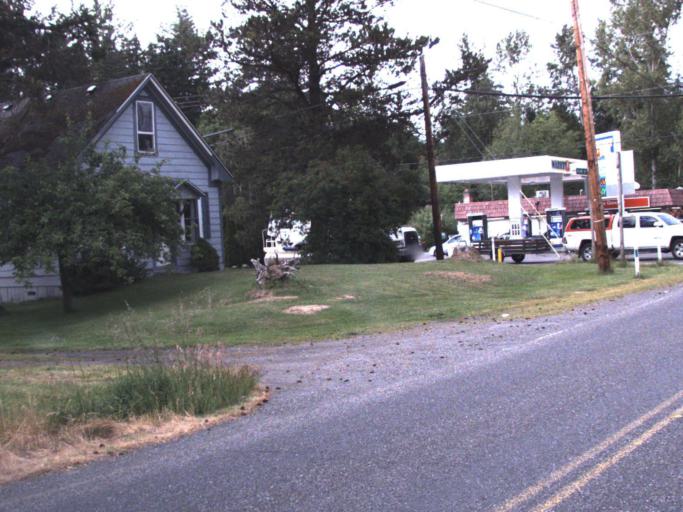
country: US
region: Washington
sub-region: Whatcom County
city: Blaine
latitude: 48.9619
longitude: -122.7300
